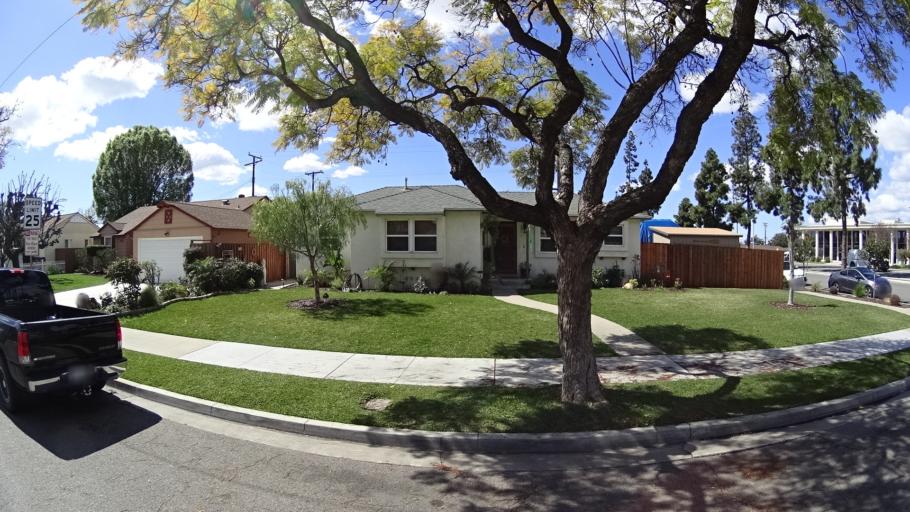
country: US
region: California
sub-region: Orange County
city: Anaheim
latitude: 33.8399
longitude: -117.8922
